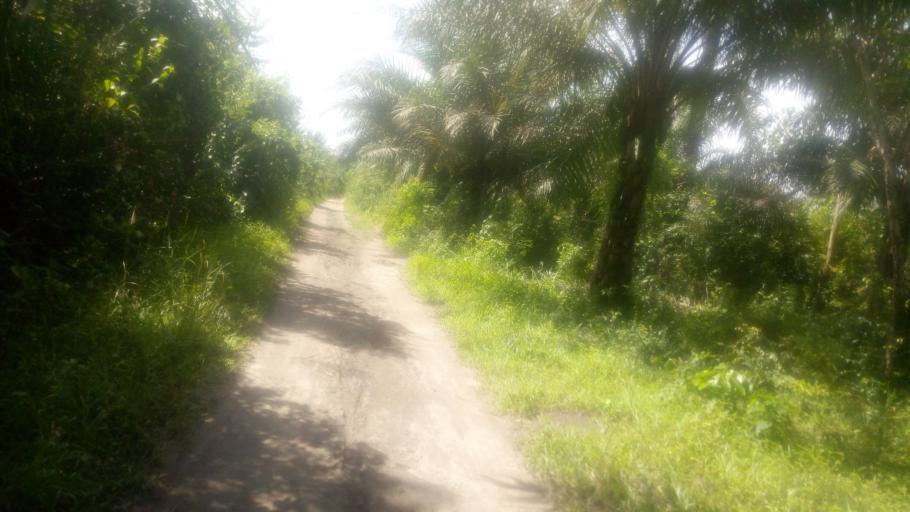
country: SL
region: Northern Province
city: Magburaka
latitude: 8.6534
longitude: -12.0692
